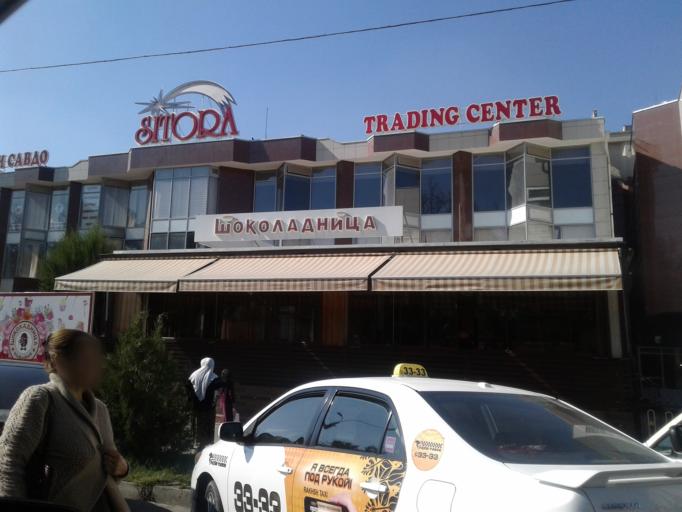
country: TJ
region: Dushanbe
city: Dushanbe
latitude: 38.5704
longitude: 68.7879
